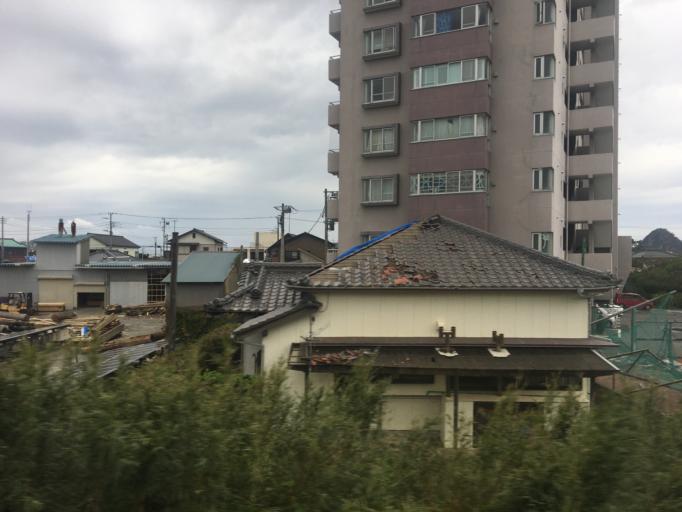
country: JP
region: Chiba
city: Tateyama
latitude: 35.0950
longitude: 139.8495
